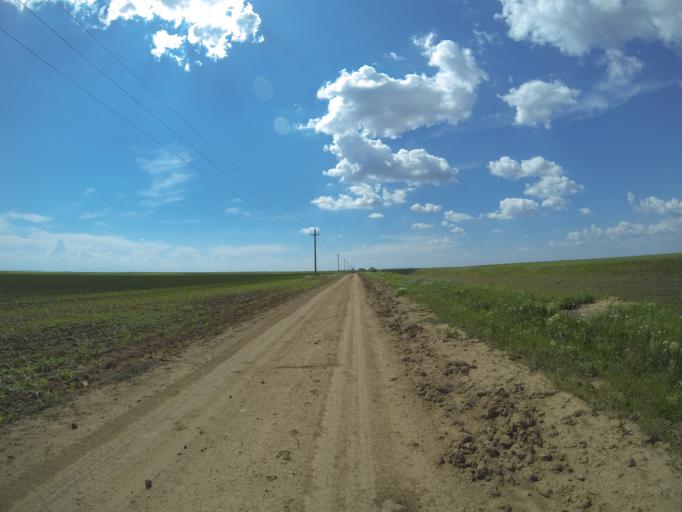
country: RO
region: Dolj
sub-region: Comuna Dranicu
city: Dranic
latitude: 44.0176
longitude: 23.7770
